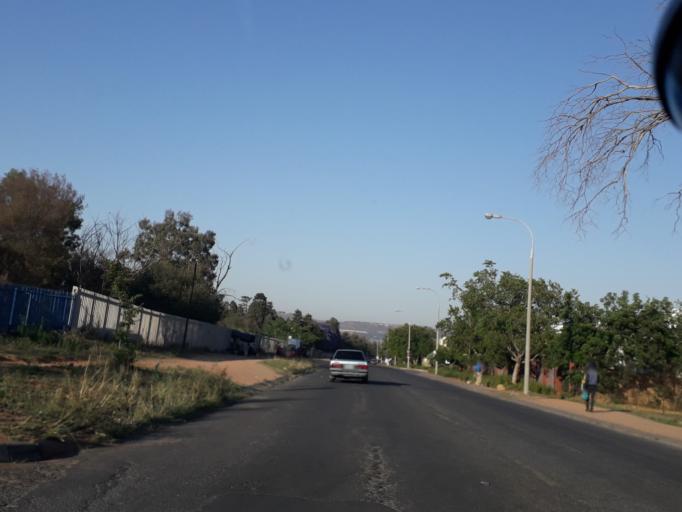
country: ZA
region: Gauteng
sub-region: West Rand District Municipality
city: Muldersdriseloop
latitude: -26.0792
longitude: 27.9211
